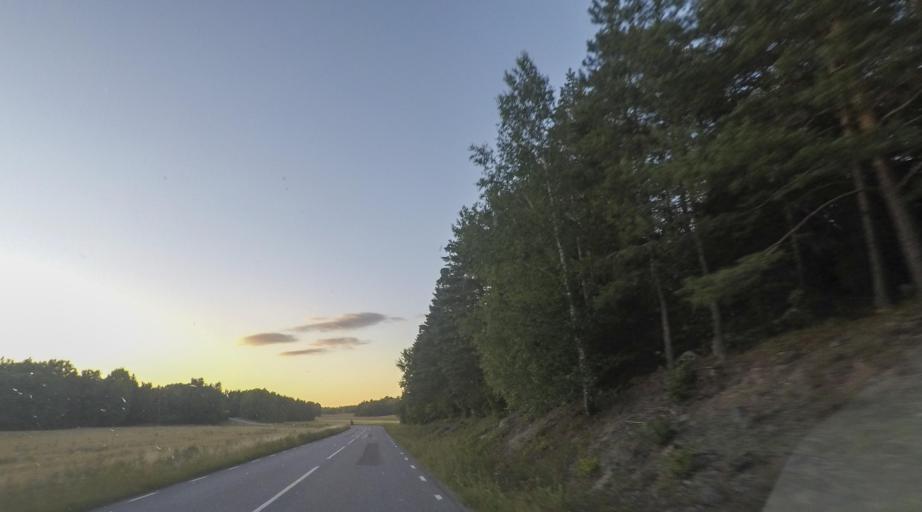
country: SE
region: Soedermanland
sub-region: Trosa Kommun
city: Trosa
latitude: 58.9769
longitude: 17.6927
